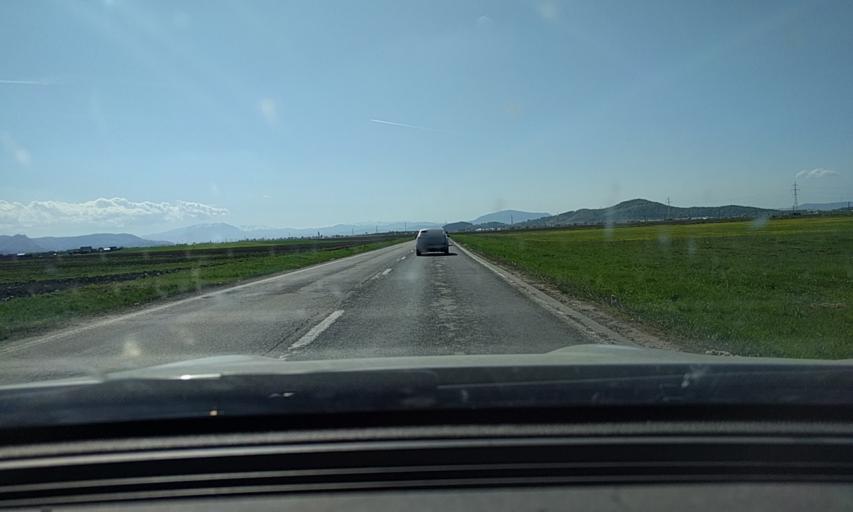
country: RO
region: Brasov
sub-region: Comuna Prejmer
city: Prejmer
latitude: 45.7141
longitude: 25.7304
